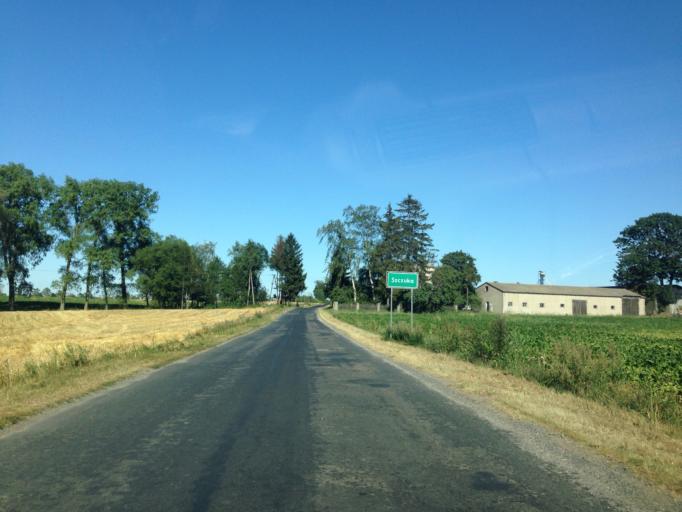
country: PL
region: Kujawsko-Pomorskie
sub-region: Powiat brodnicki
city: Brodnica
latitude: 53.2077
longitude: 19.4274
